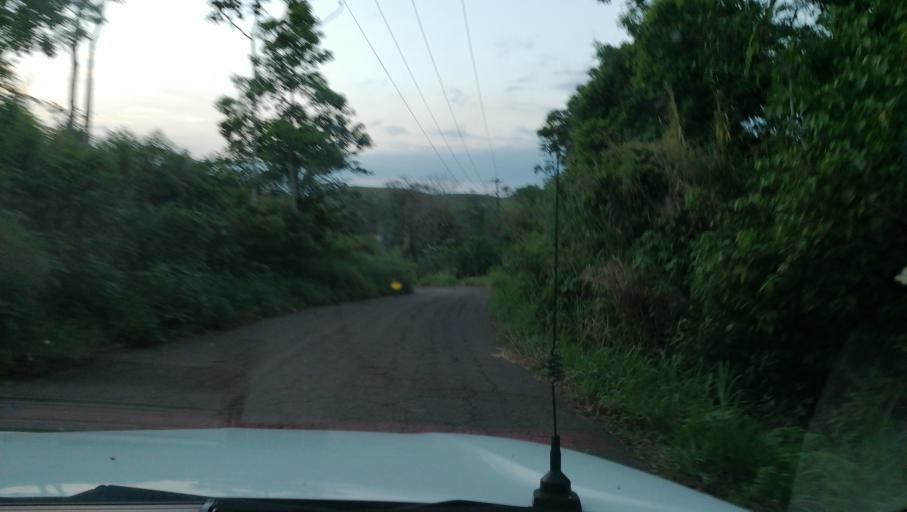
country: MX
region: Chiapas
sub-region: Ostuacan
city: Nuevo Juan del Grijalva
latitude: 17.4429
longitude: -93.3529
